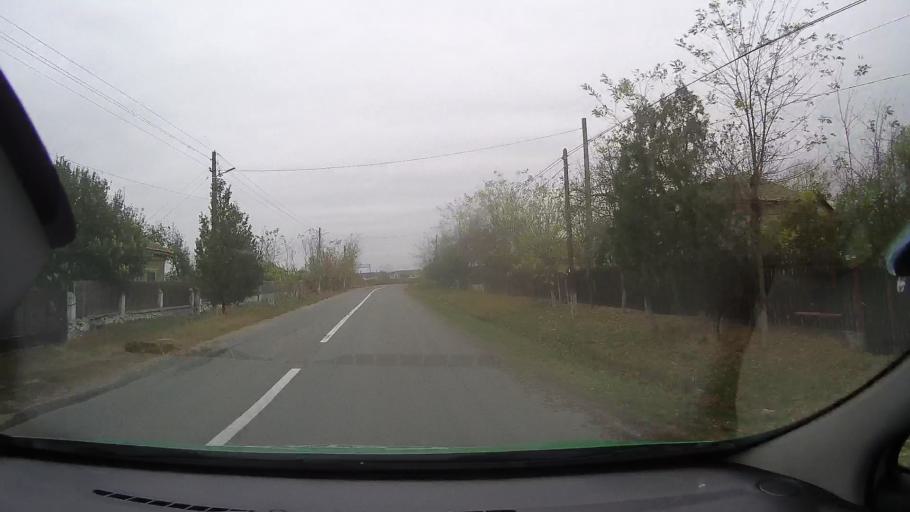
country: RO
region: Constanta
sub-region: Comuna Crucea
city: Crucea
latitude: 44.4498
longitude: 28.2421
